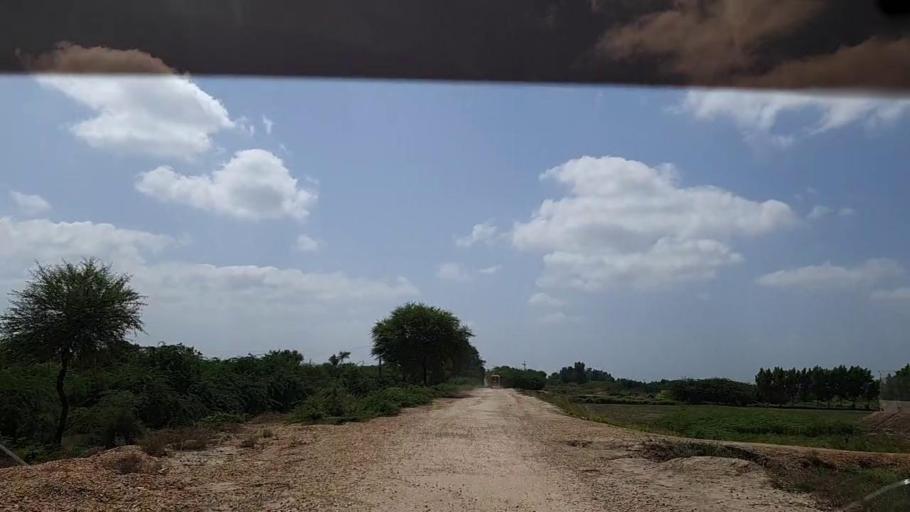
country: PK
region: Sindh
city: Badin
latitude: 24.5801
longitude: 68.7841
